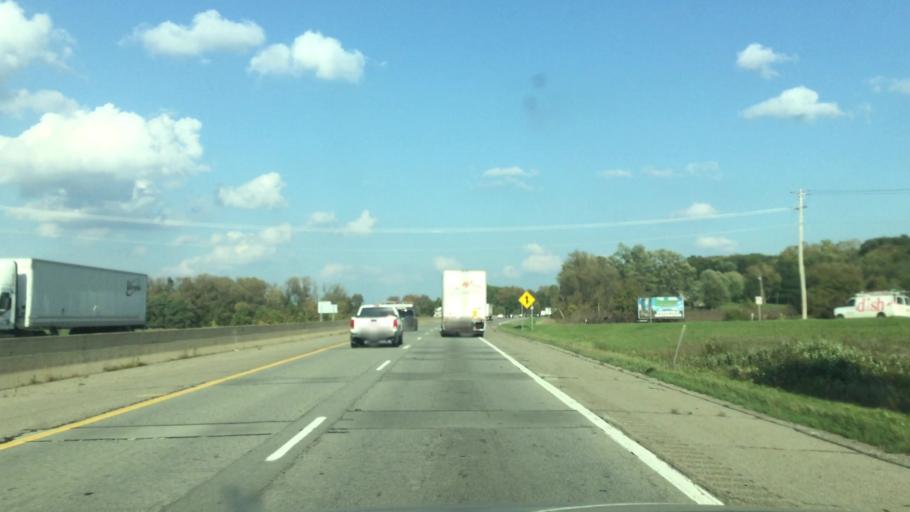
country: US
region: Michigan
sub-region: Jackson County
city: Spring Arbor
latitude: 42.2666
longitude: -84.6186
